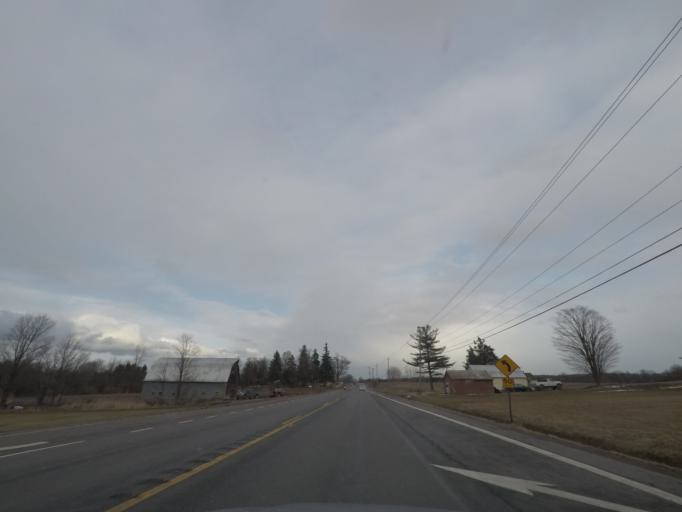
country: US
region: New York
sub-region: Oneida County
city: Vernon
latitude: 43.0724
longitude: -75.4900
